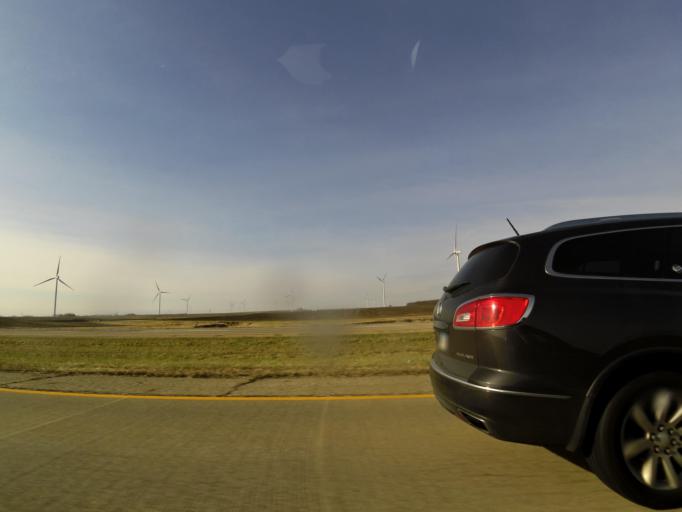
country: US
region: Illinois
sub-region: Macon County
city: Forsyth
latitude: 39.9804
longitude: -88.9560
